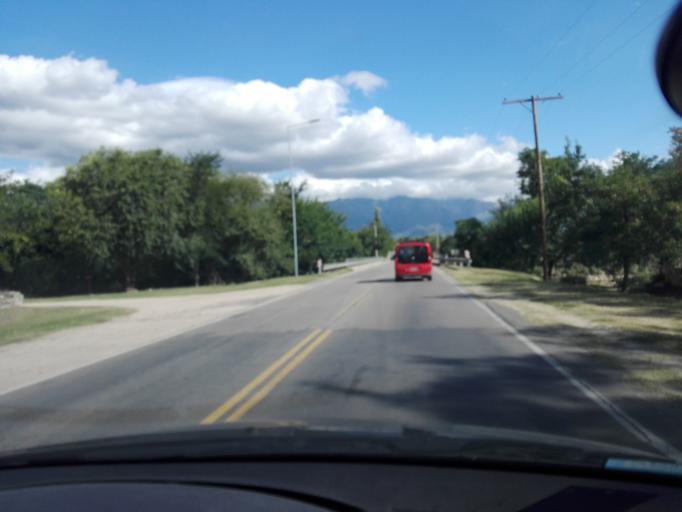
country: AR
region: Cordoba
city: Mina Clavero
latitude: -31.8038
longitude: -65.0049
